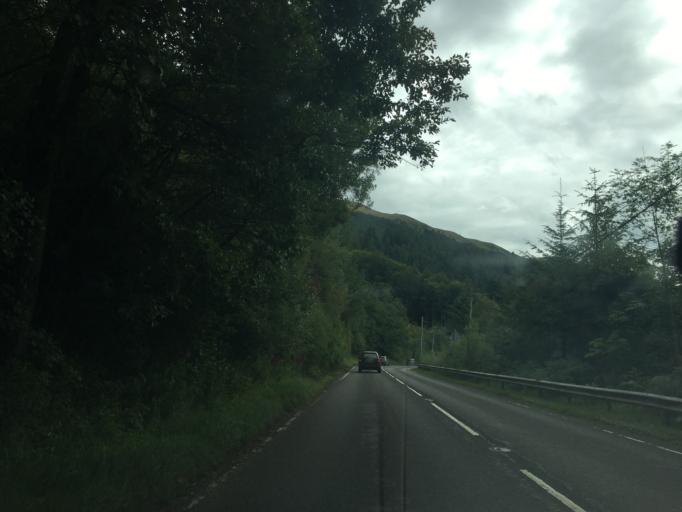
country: GB
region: Scotland
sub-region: Stirling
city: Callander
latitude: 56.2930
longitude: -4.2894
